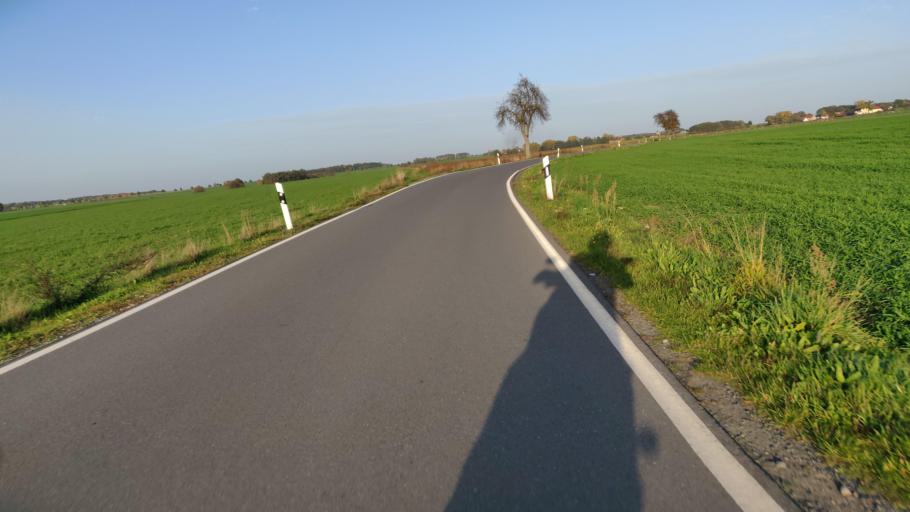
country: DE
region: Brandenburg
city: Hirschfeld
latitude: 51.3435
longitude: 13.6050
